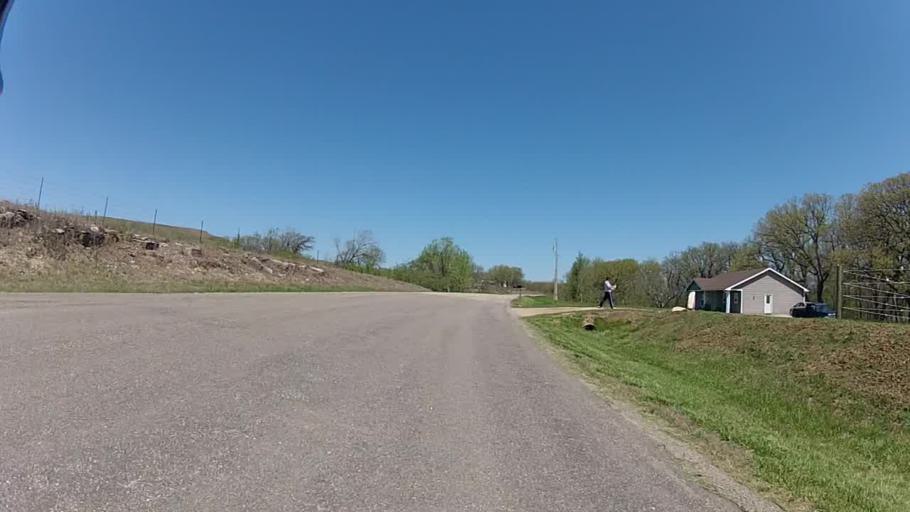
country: US
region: Kansas
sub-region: Riley County
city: Ogden
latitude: 38.9890
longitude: -96.5965
